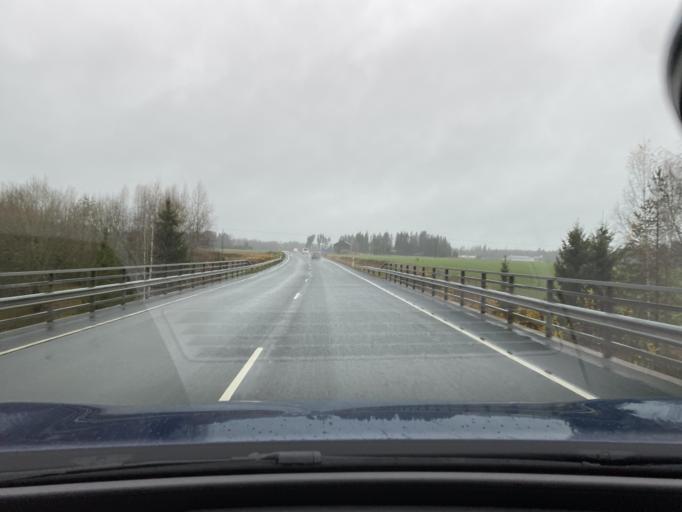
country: FI
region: Varsinais-Suomi
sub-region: Loimaa
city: Alastaro
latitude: 60.9324
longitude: 22.8719
